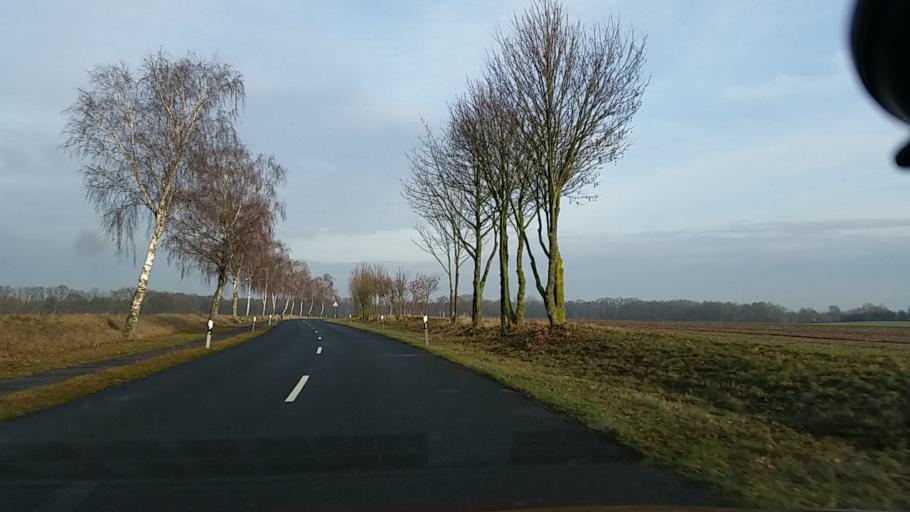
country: DE
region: Lower Saxony
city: Luder
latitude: 52.8166
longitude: 10.6750
